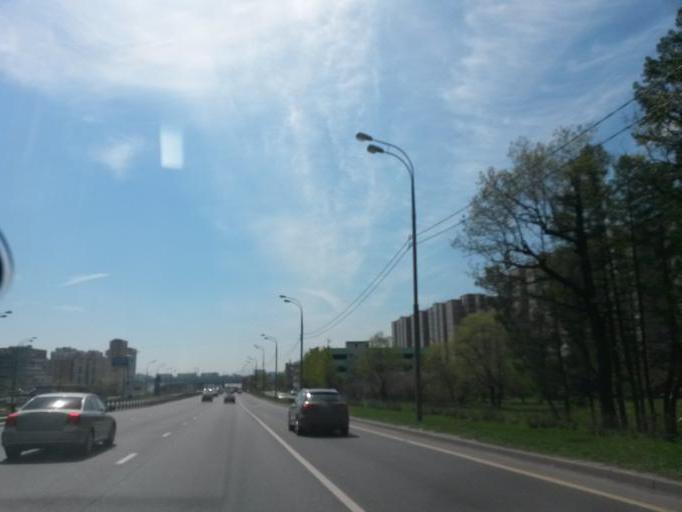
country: RU
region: Moskovskaya
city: Shcherbinka
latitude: 55.5394
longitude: 37.5831
